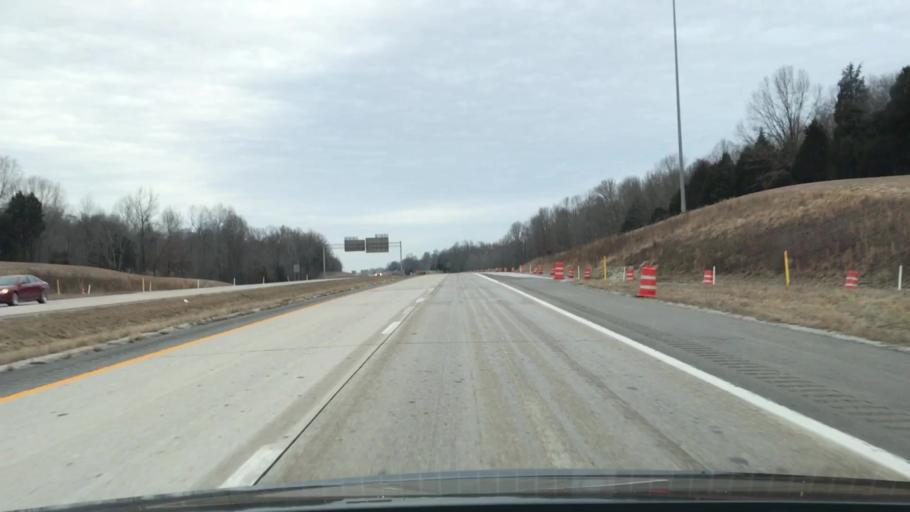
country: US
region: Kentucky
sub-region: Ohio County
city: Beaver Dam
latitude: 37.3878
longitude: -86.8108
